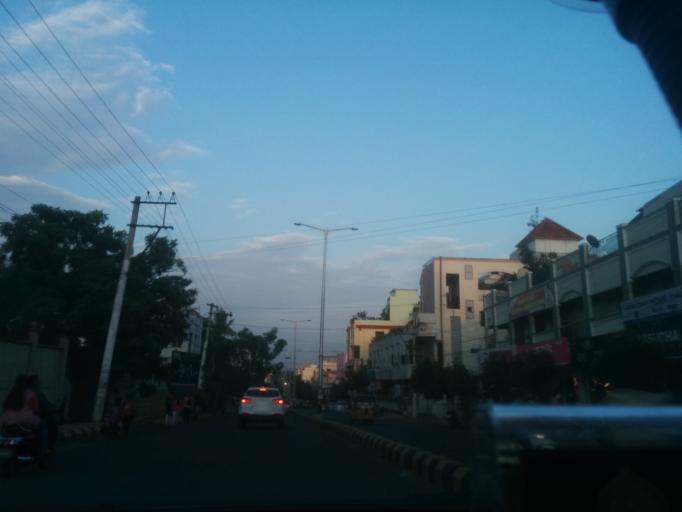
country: IN
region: Andhra Pradesh
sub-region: East Godavari
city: Rajahmundry
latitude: 17.0077
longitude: 81.7938
